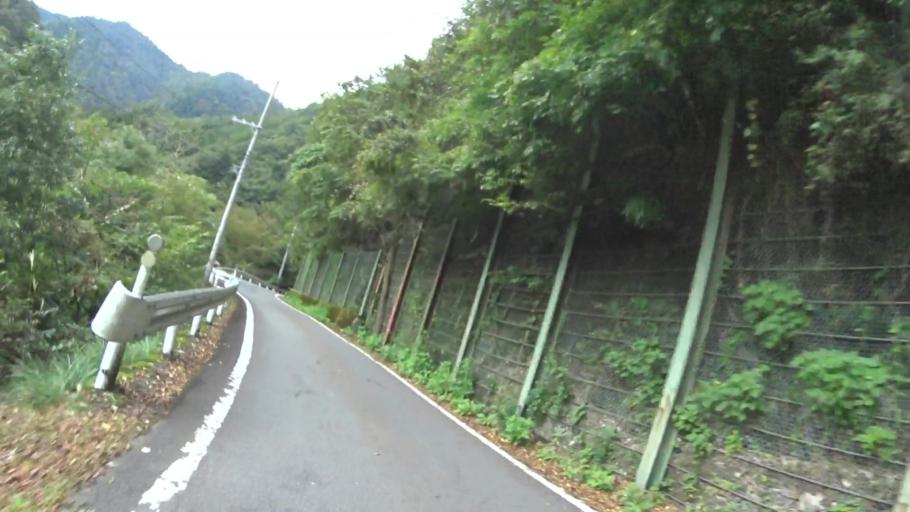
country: JP
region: Fukui
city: Obama
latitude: 35.3124
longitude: 135.6922
